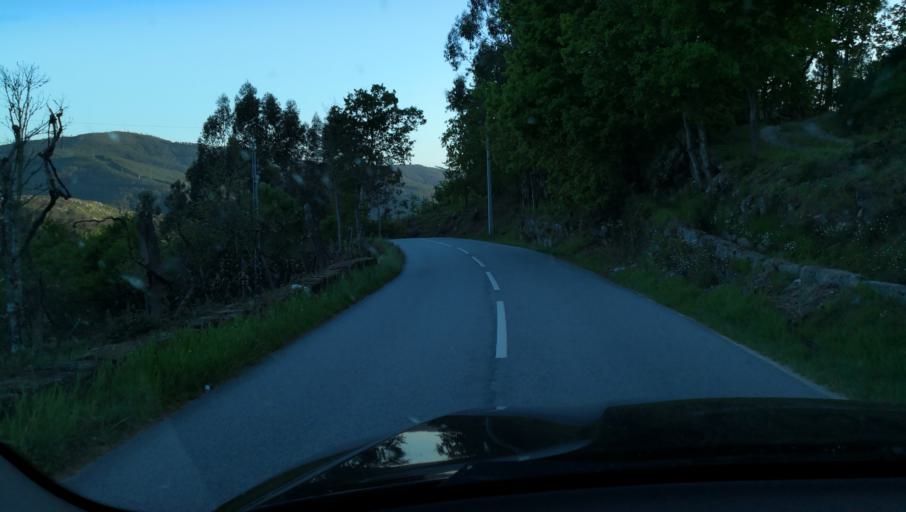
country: PT
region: Vila Real
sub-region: Mondim de Basto
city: Mondim de Basto
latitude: 41.4137
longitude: -7.8960
